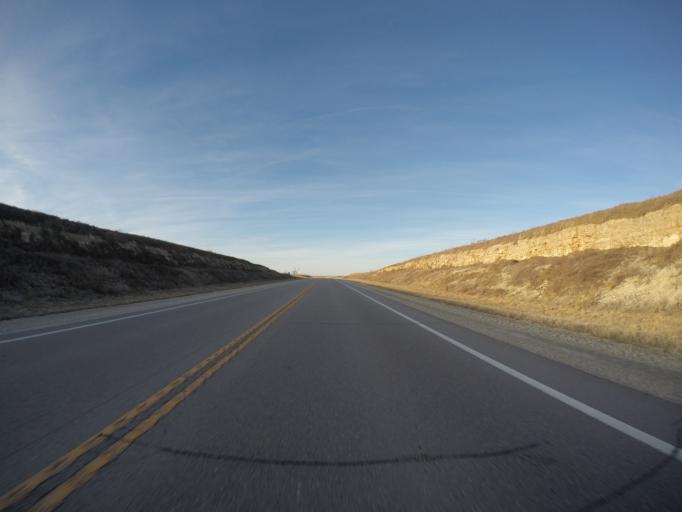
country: US
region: Kansas
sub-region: Marion County
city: Marion
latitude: 38.2867
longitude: -96.9645
